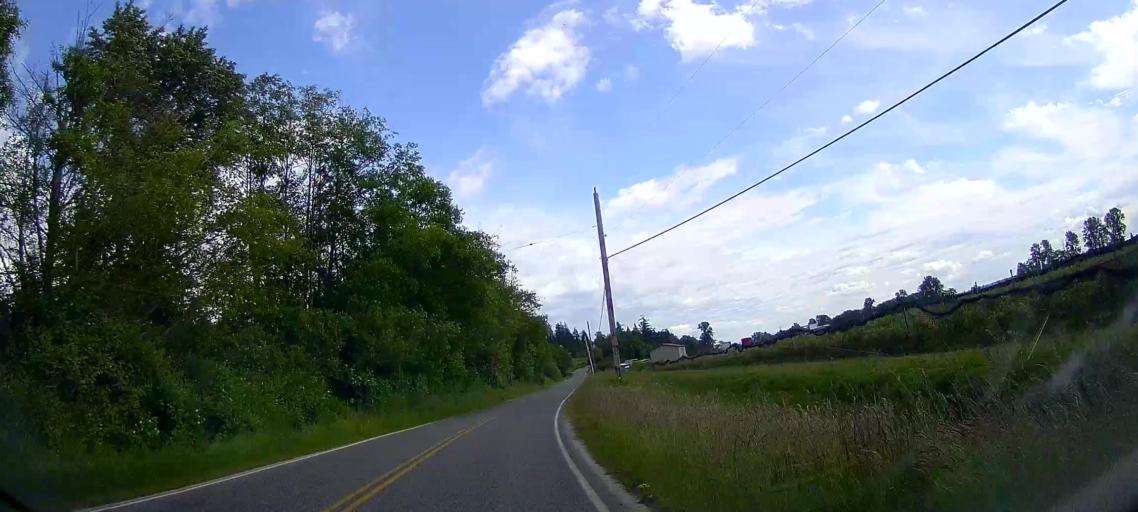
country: US
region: Washington
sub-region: Skagit County
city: Burlington
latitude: 48.5811
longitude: -122.4029
